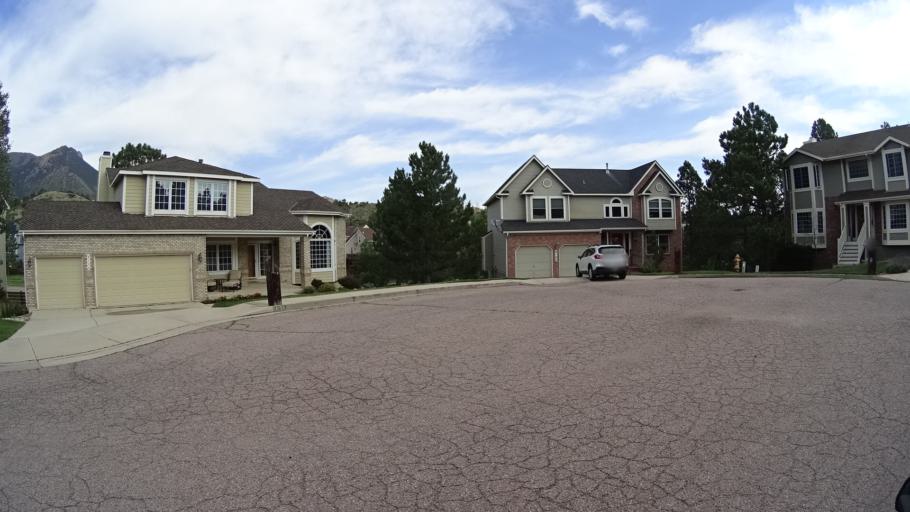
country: US
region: Colorado
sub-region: El Paso County
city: Air Force Academy
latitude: 38.9494
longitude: -104.8655
